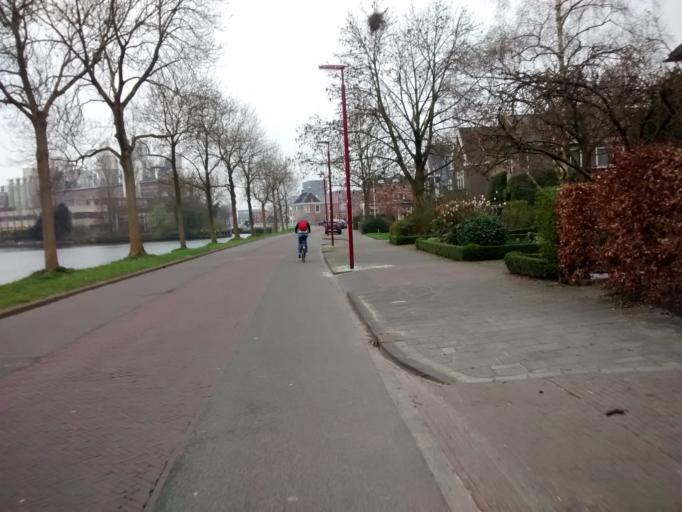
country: NL
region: Utrecht
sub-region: Gemeente Nieuwegein
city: Nieuwegein
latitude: 52.0339
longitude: 5.0919
